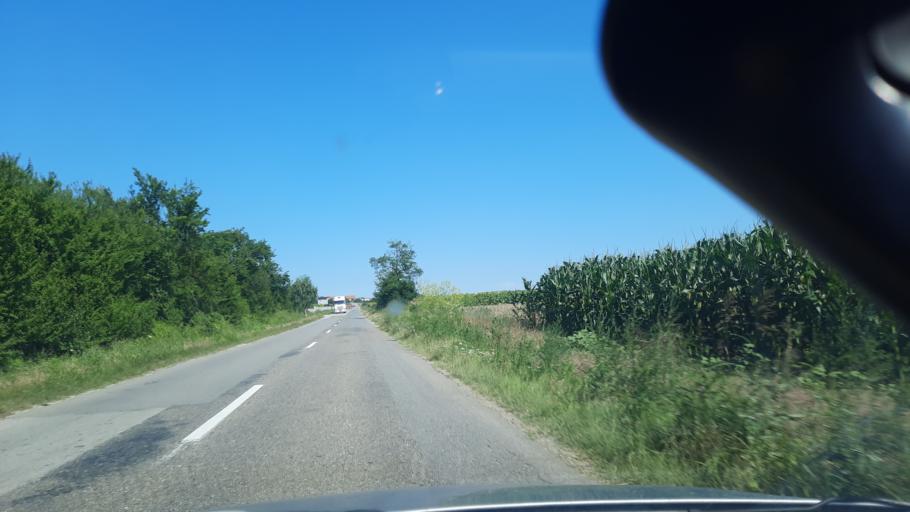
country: RS
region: Central Serbia
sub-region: Branicevski Okrug
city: Malo Crnice
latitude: 44.5755
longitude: 21.3465
